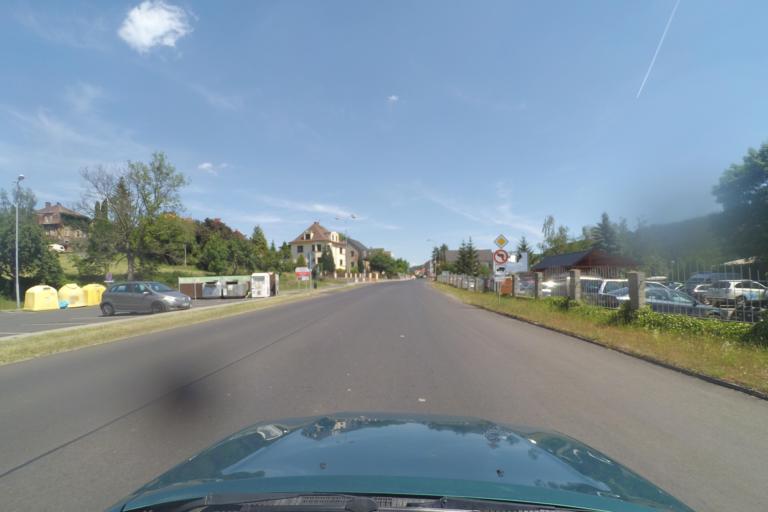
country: CZ
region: Ustecky
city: Benesov nad Ploucnici
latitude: 50.7412
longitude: 14.2959
